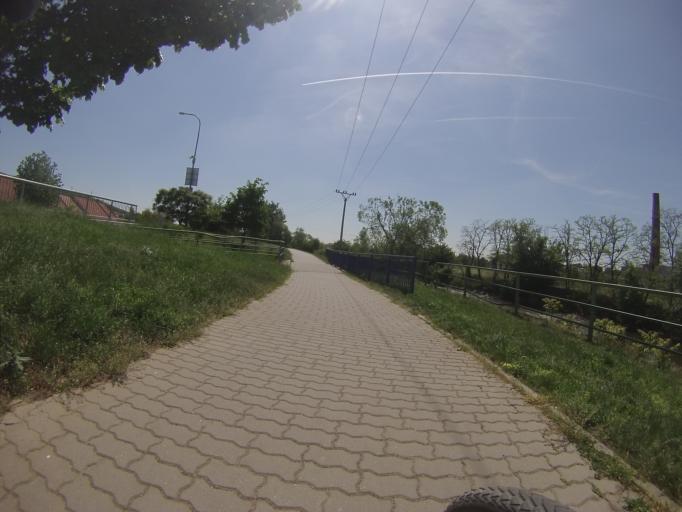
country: CZ
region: South Moravian
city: Zidlochovice
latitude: 49.0352
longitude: 16.6170
